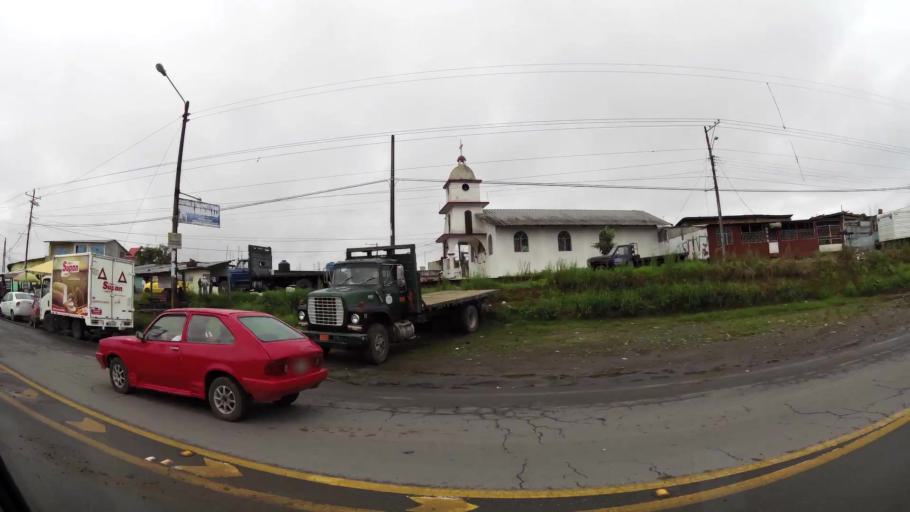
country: EC
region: Santo Domingo de los Tsachilas
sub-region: Canton Santo Domingo de los Colorados
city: Santo Domingo de los Colorados
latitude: -0.2724
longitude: -79.1996
